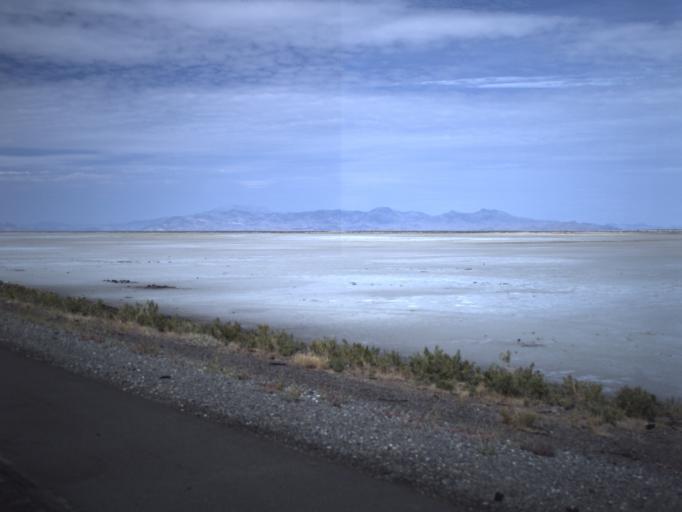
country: US
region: Utah
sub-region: Tooele County
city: Wendover
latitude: 40.7308
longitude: -113.4559
